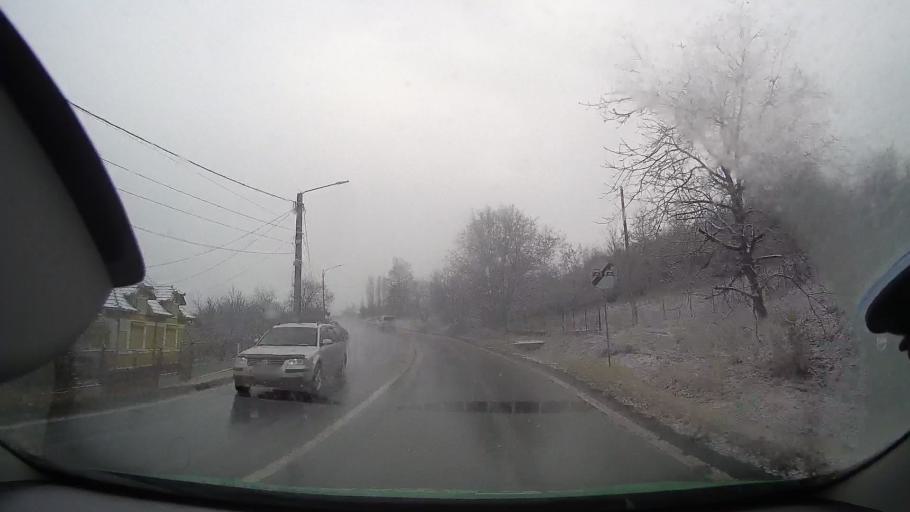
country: RO
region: Mures
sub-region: Comuna Bagaciu
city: Delenii
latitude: 46.2687
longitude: 24.2993
